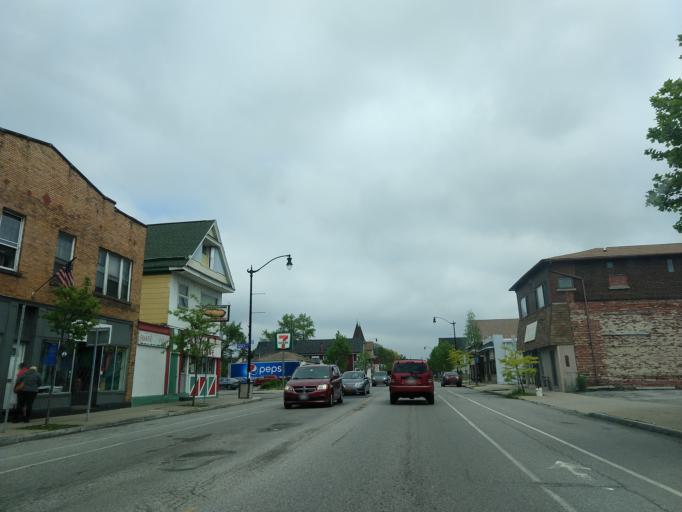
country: US
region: New York
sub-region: Erie County
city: Lackawanna
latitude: 42.8446
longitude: -78.8237
